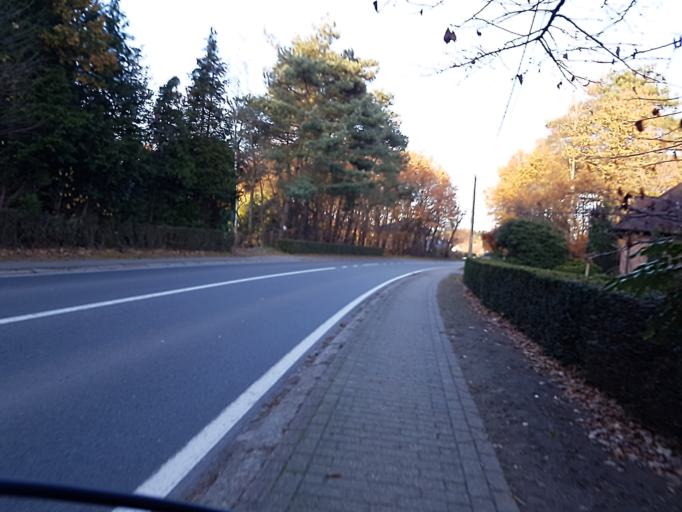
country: BE
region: Flanders
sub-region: Provincie Vlaams-Brabant
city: Haacht
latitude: 50.9742
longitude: 4.6237
